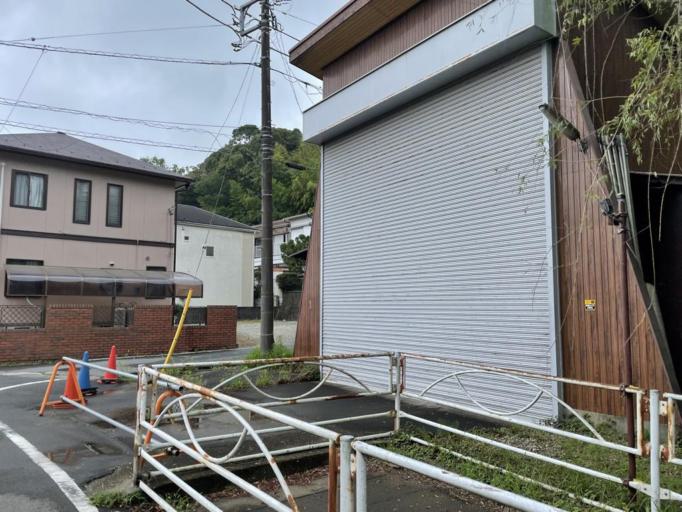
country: JP
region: Chiba
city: Sakura
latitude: 35.7250
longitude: 140.2219
